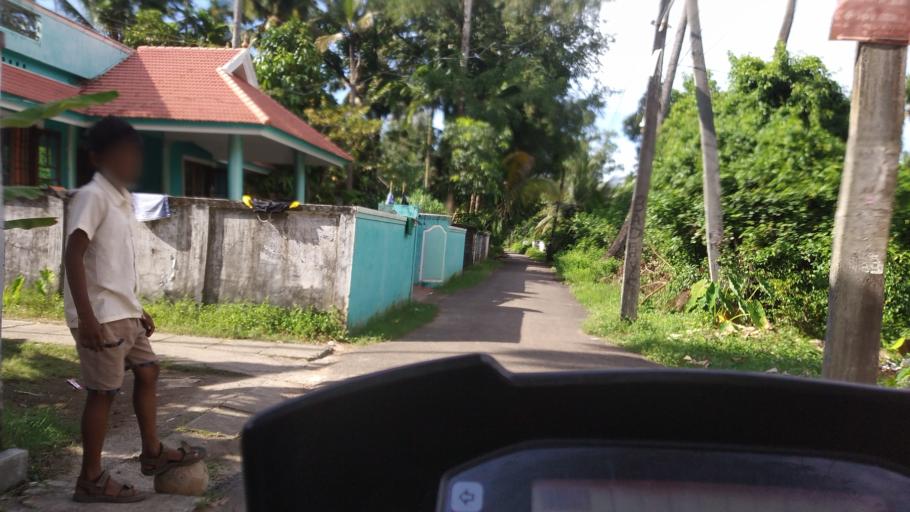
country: IN
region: Kerala
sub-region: Ernakulam
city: Elur
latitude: 10.0743
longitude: 76.2159
